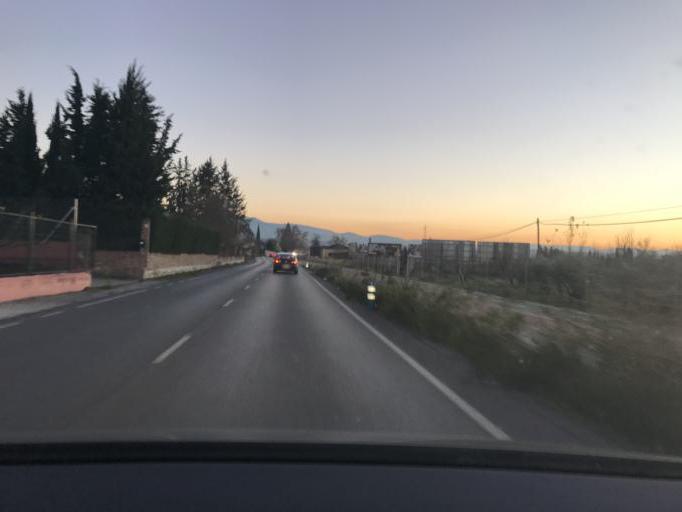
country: ES
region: Andalusia
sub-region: Provincia de Granada
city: Armilla
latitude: 37.1416
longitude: -3.6023
